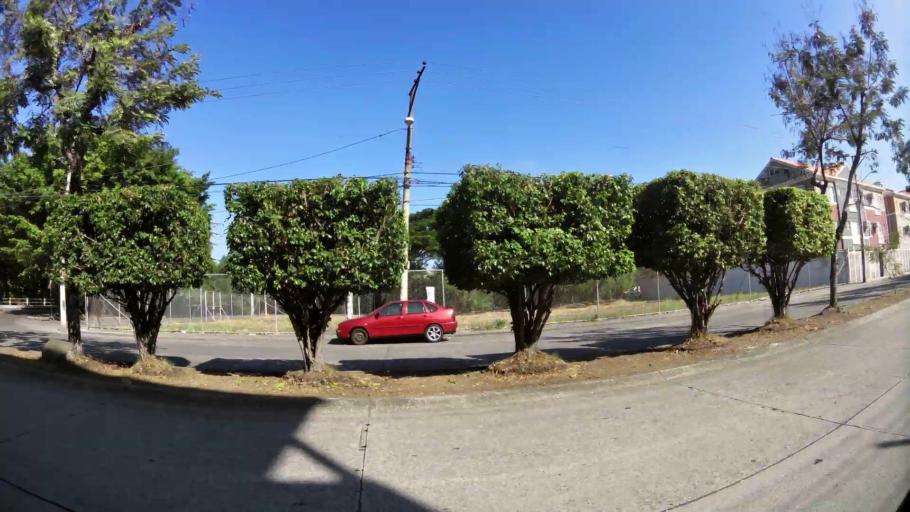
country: EC
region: Guayas
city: Guayaquil
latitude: -2.1573
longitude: -79.9021
